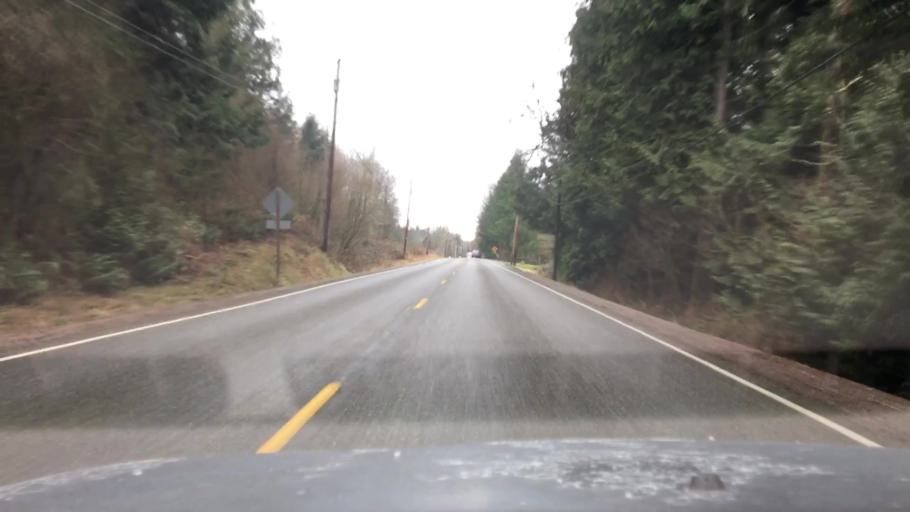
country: US
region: Washington
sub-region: Whatcom County
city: Sudden Valley
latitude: 48.6329
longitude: -122.3141
